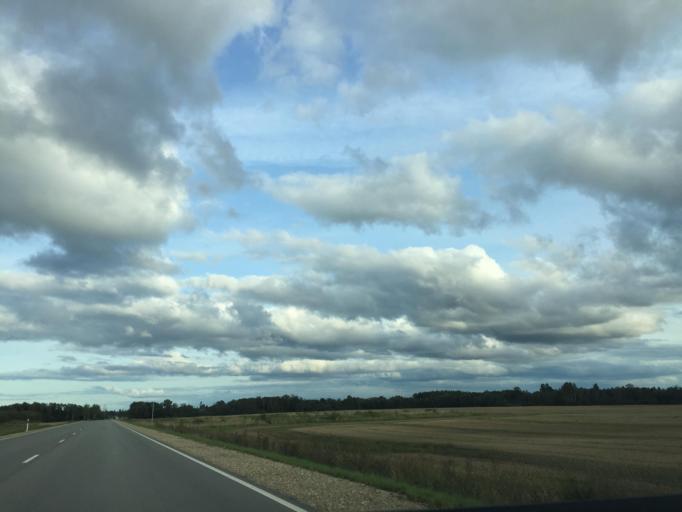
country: LV
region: Nereta
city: Nereta
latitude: 56.2489
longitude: 25.2358
